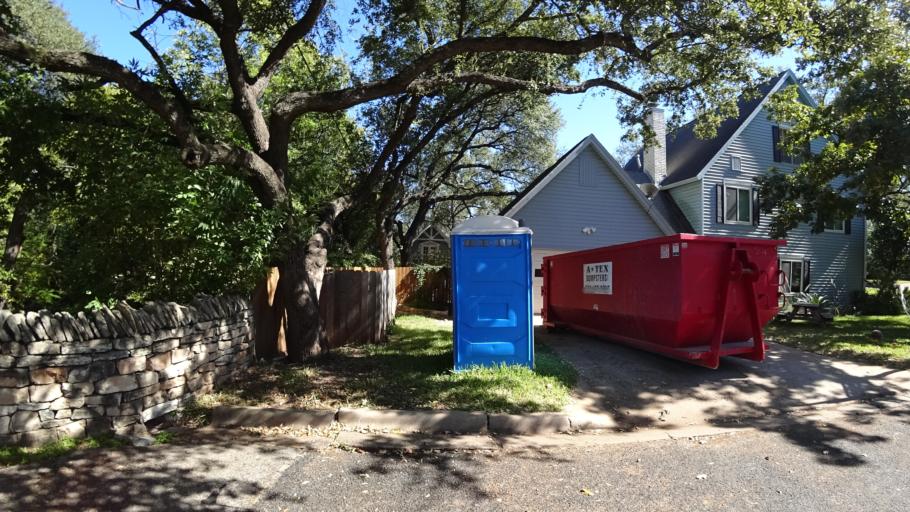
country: US
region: Texas
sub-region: Travis County
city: West Lake Hills
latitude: 30.3617
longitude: -97.7612
